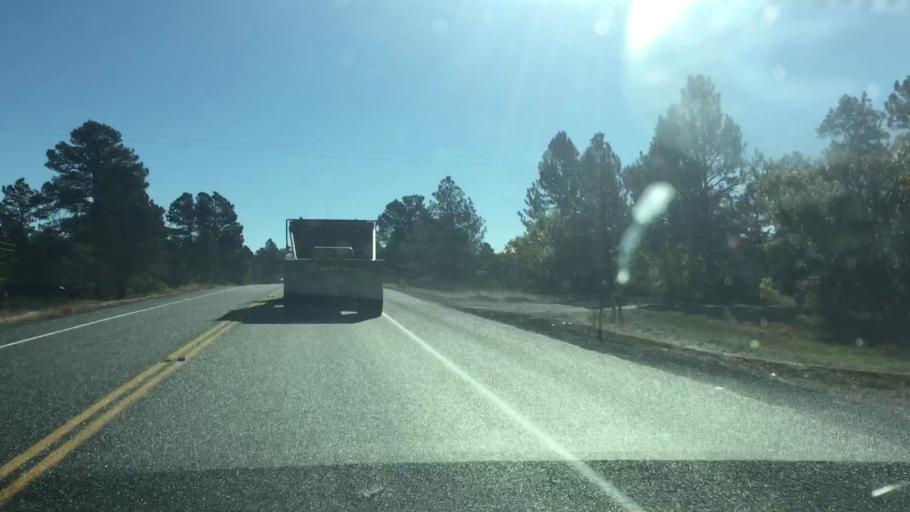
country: US
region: Colorado
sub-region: Douglas County
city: The Pinery
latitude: 39.3891
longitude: -104.7434
